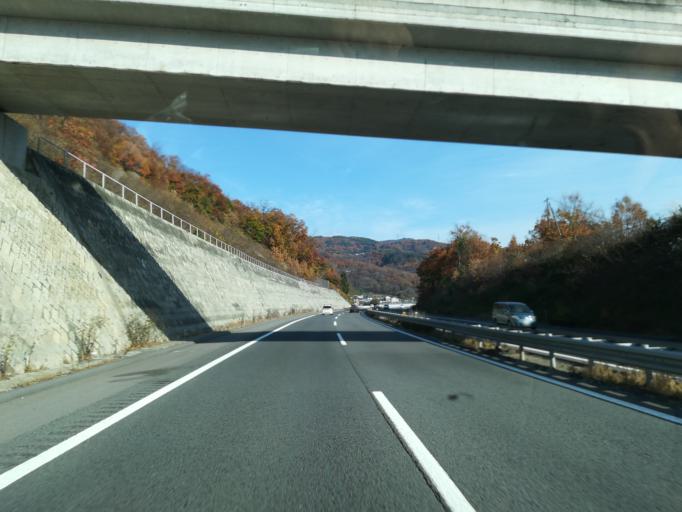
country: JP
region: Nagano
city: Ueda
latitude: 36.4099
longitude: 138.2996
